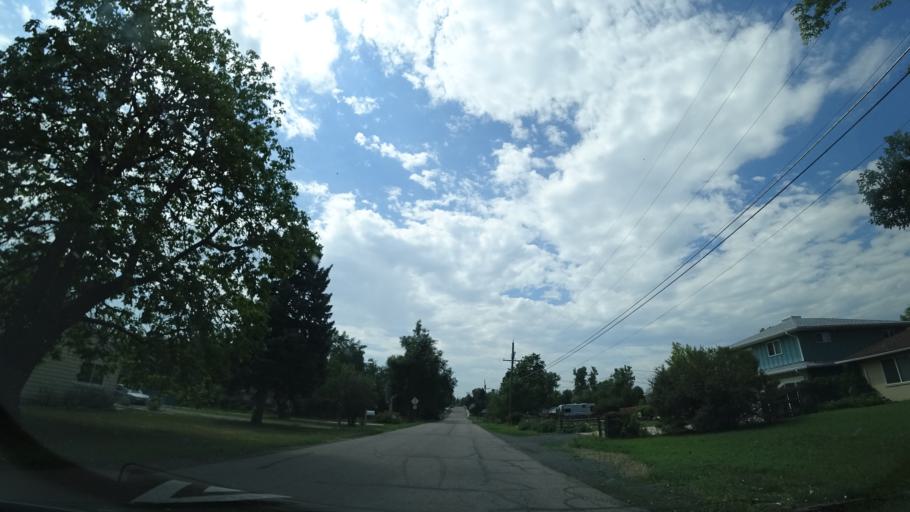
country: US
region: Colorado
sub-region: Jefferson County
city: Lakewood
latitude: 39.7145
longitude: -105.0674
